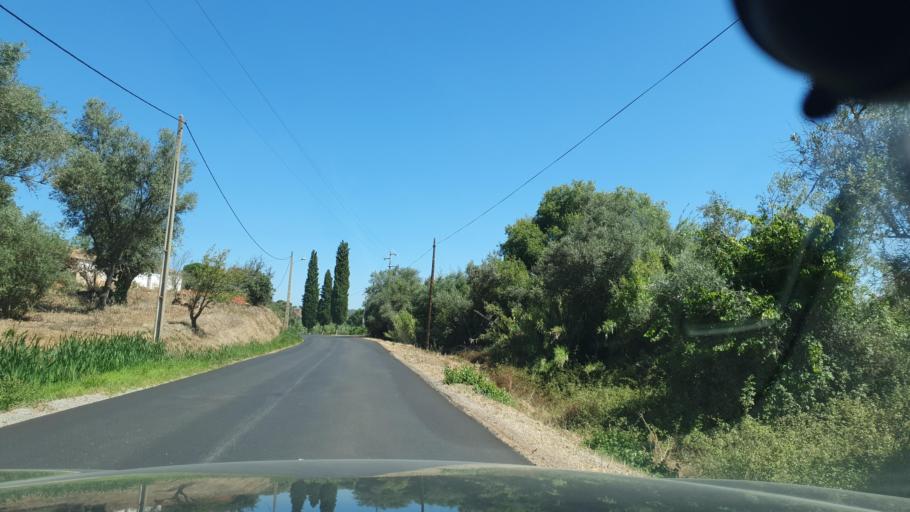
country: PT
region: Faro
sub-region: Monchique
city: Monchique
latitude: 37.4652
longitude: -8.4879
